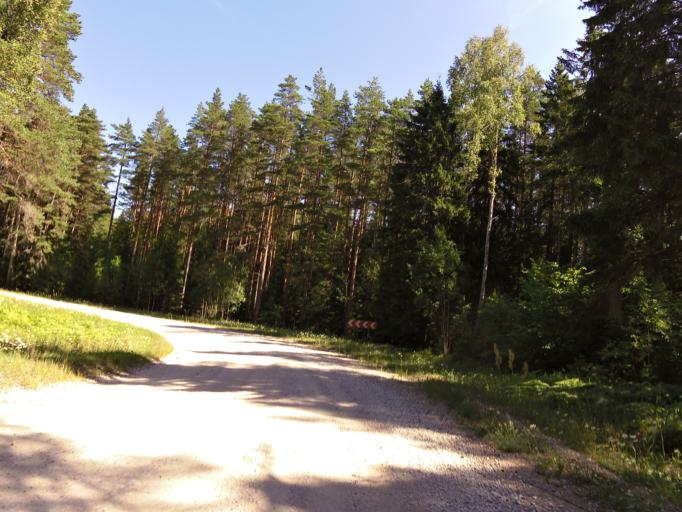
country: EE
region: Hiiumaa
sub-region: Kaerdla linn
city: Kardla
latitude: 58.9189
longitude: 22.3503
